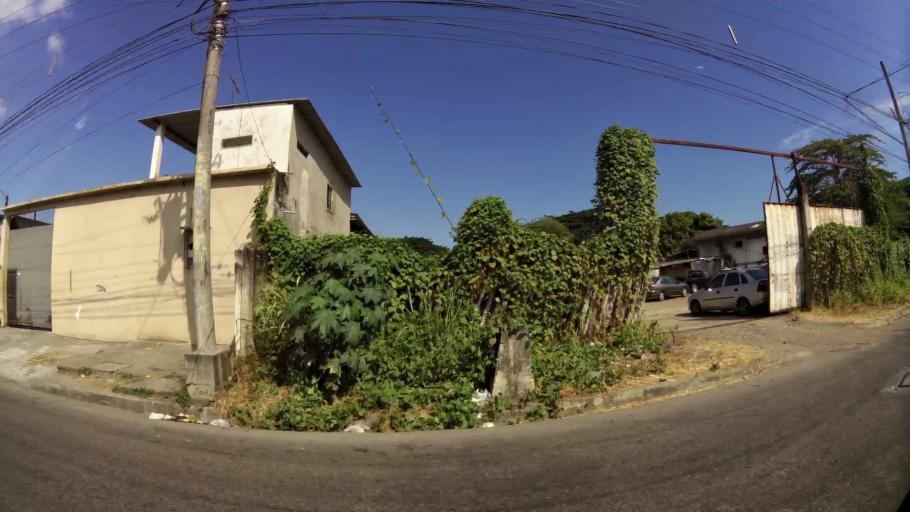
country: EC
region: Guayas
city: Guayaquil
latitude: -2.1588
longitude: -79.9393
